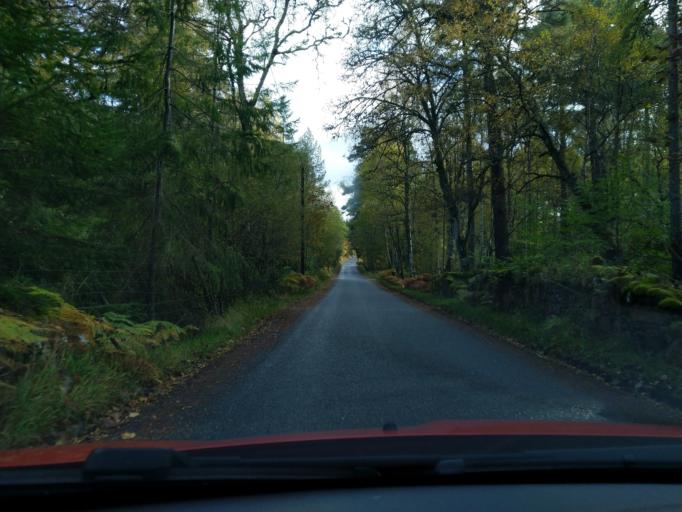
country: GB
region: Scotland
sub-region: Perth and Kinross
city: Aberfeldy
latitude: 56.7080
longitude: -4.0813
